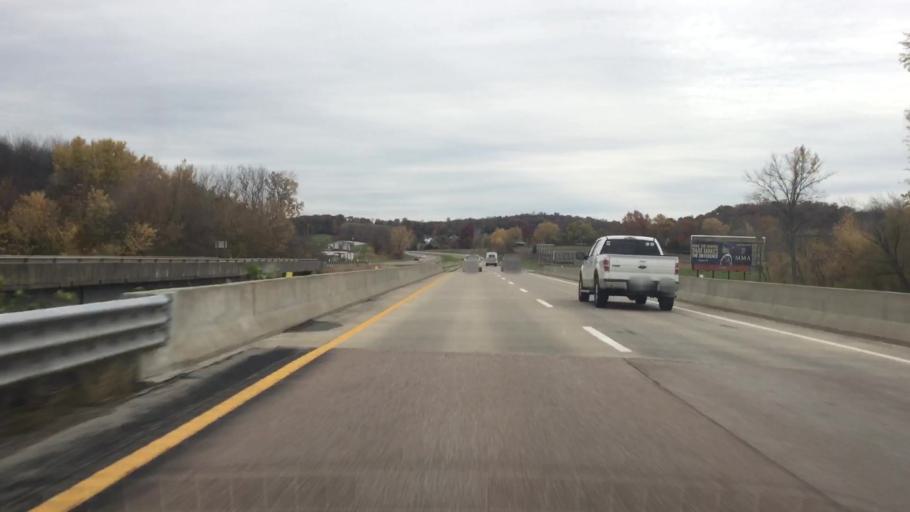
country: US
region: Missouri
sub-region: Cole County
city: Jefferson City
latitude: 38.6449
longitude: -92.2012
